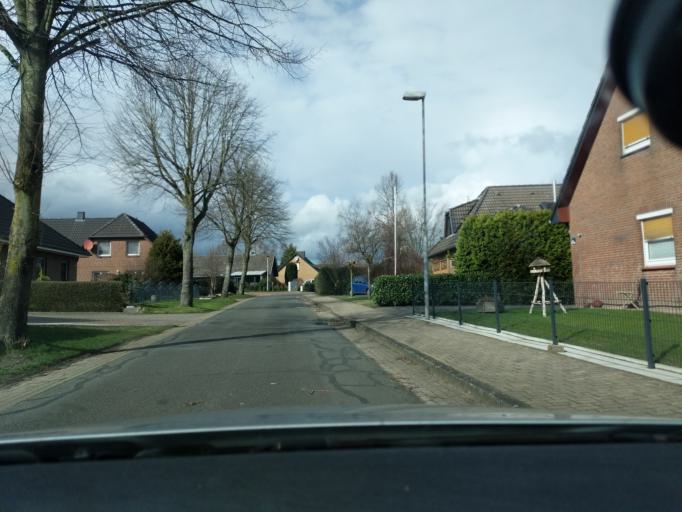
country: DE
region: Lower Saxony
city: Oldendorf
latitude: 53.5856
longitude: 9.2399
